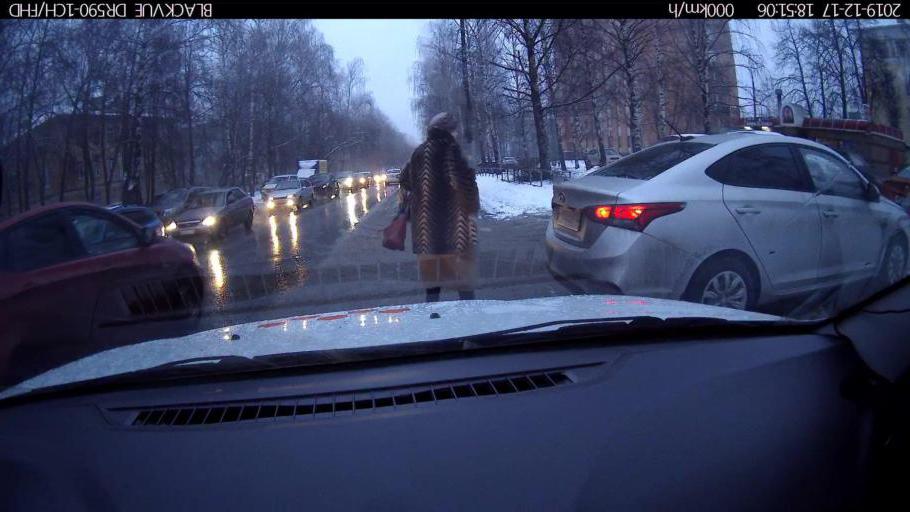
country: RU
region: Nizjnij Novgorod
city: Nizhniy Novgorod
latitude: 56.2818
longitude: 43.9846
